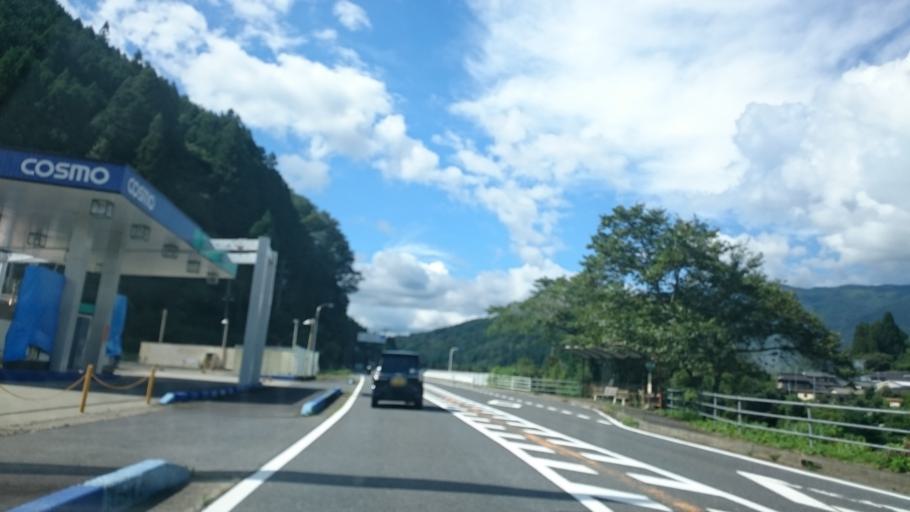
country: JP
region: Gifu
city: Nakatsugawa
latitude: 35.6213
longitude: 137.4620
